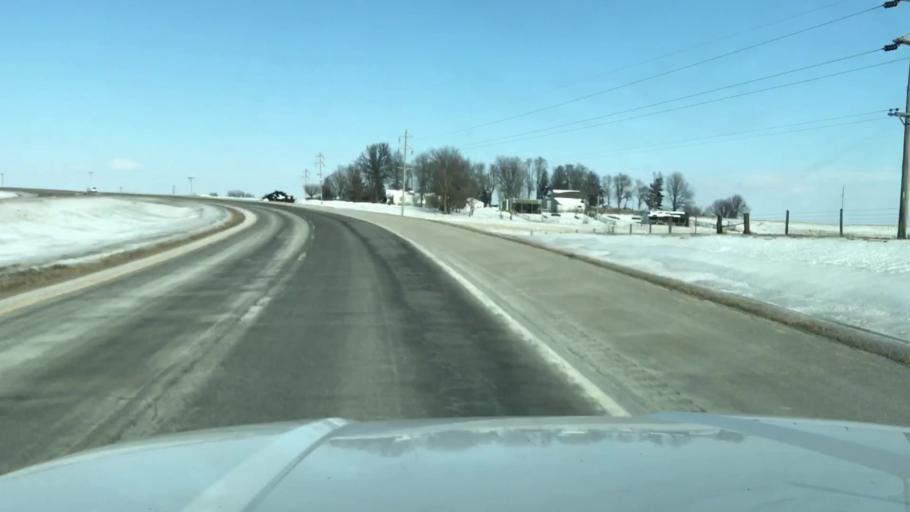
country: US
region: Missouri
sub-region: Nodaway County
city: Maryville
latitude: 40.2701
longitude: -94.8664
